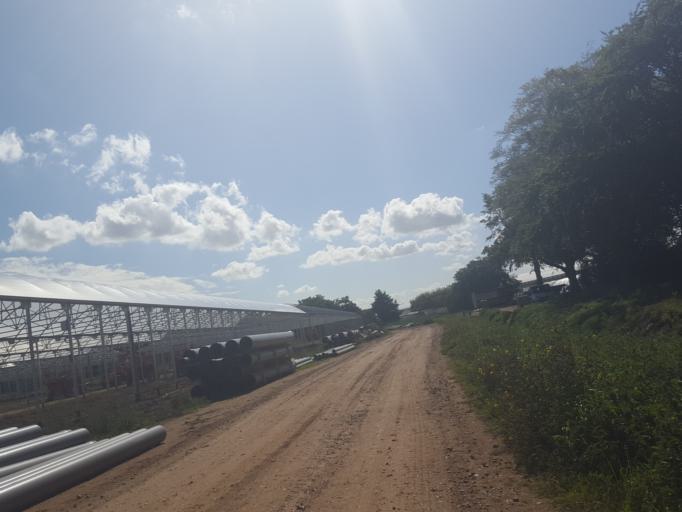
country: GB
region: England
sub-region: Essex
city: Alresford
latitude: 51.8555
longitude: 1.0287
